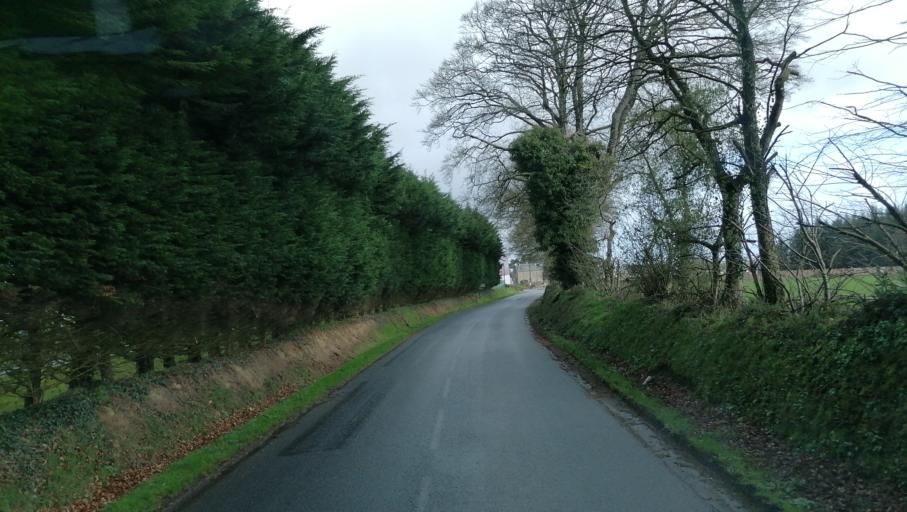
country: FR
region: Brittany
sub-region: Departement des Cotes-d'Armor
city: Lanrodec
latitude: 48.5130
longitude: -3.0311
